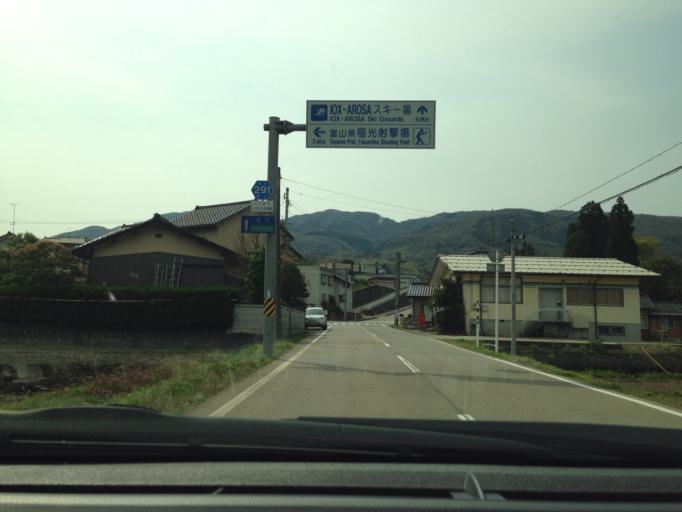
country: JP
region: Toyama
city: Fukumitsu
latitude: 36.5226
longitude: 136.8495
